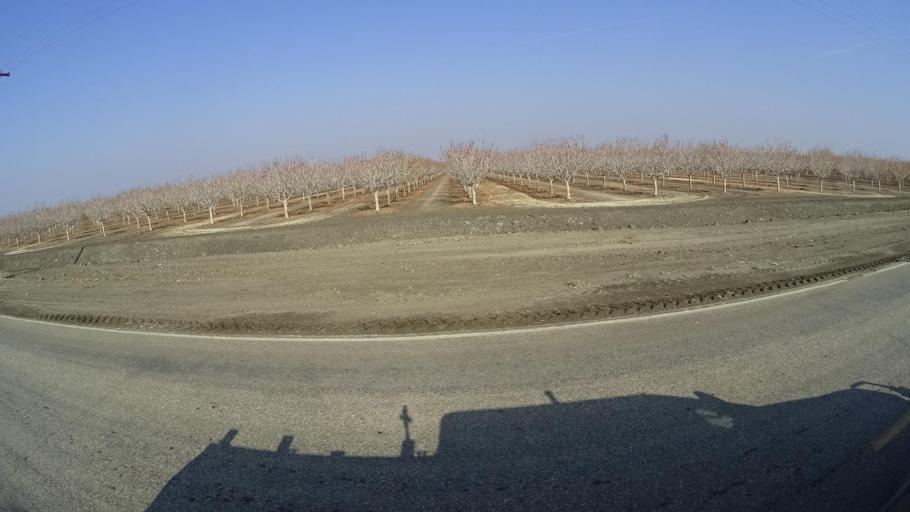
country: US
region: California
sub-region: Kern County
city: Buttonwillow
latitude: 35.3545
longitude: -119.4376
